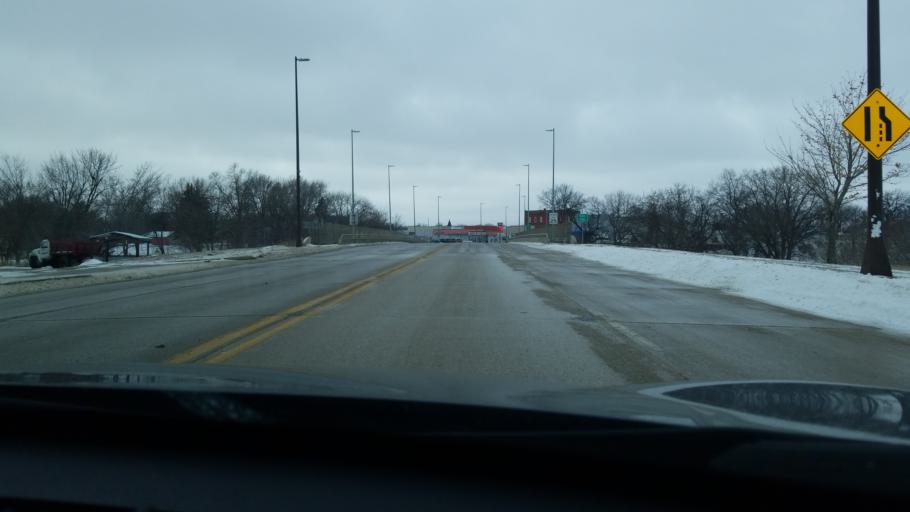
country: US
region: Iowa
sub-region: Lyon County
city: Rock Rapids
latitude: 43.4323
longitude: -96.1631
